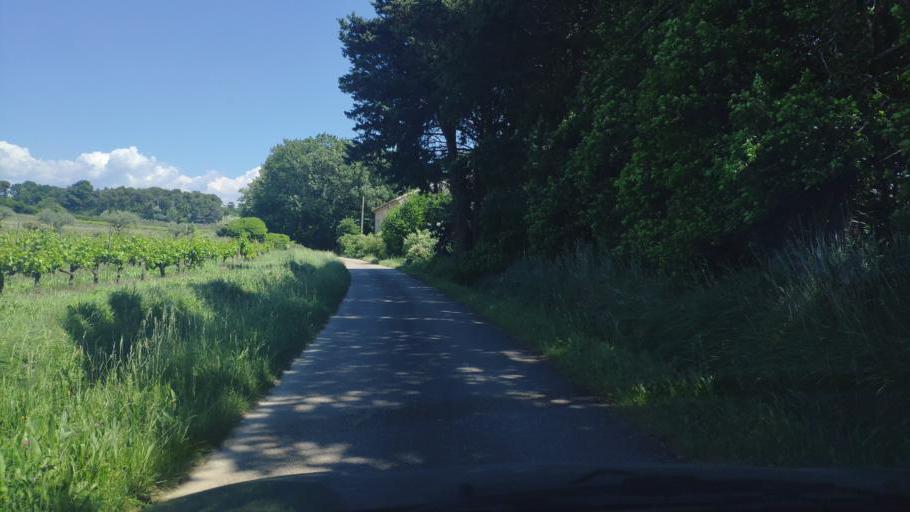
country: FR
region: Provence-Alpes-Cote d'Azur
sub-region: Departement du Vaucluse
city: Aubignan
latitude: 44.0766
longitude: 5.0309
